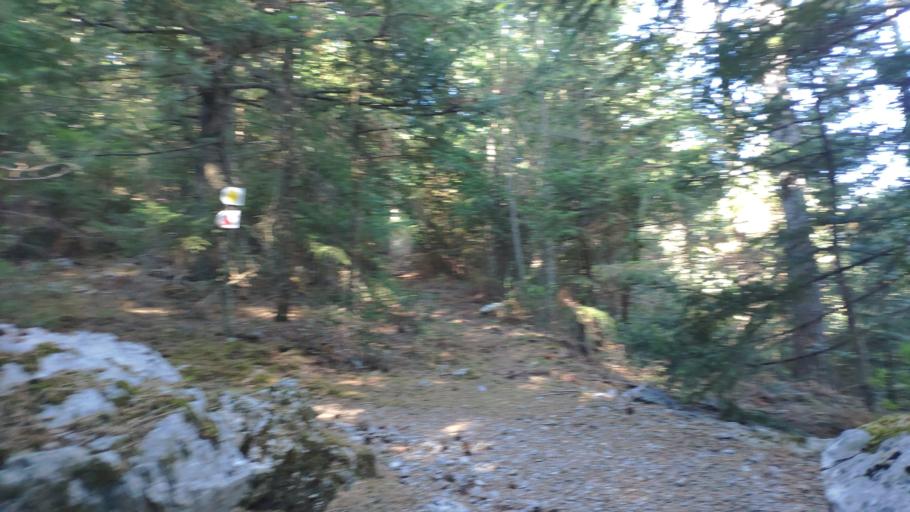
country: GR
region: Peloponnese
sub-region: Nomos Lakonias
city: Kariai
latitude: 37.1744
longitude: 22.5997
